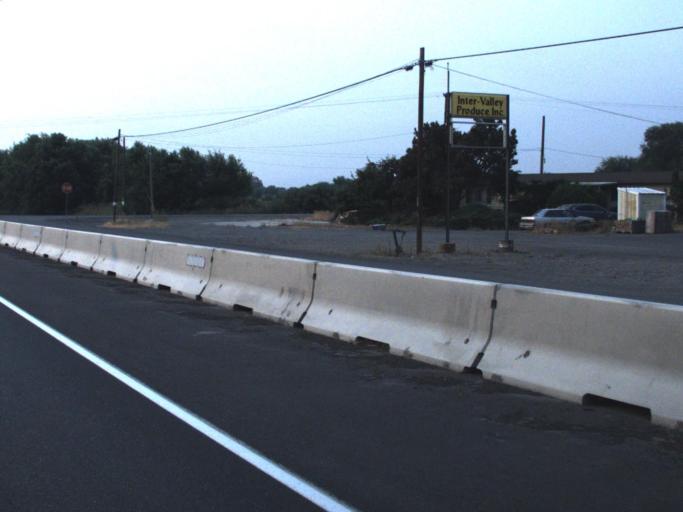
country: US
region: Washington
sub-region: Yakima County
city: Wapato
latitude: 46.4634
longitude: -120.4359
